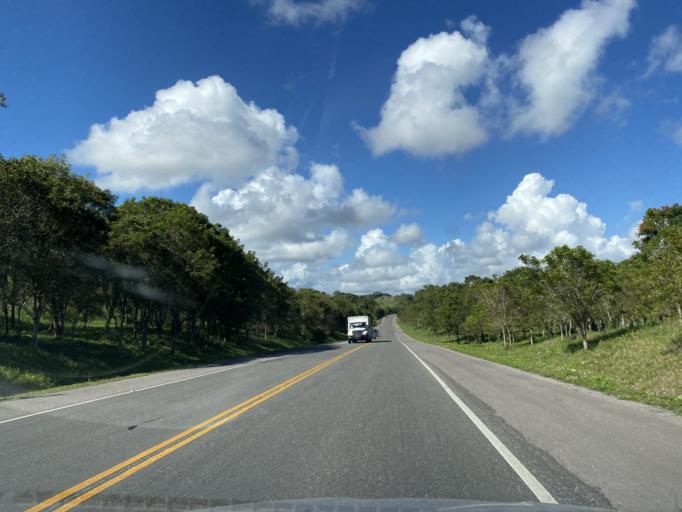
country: DO
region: Monte Plata
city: Majagual
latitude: 19.0277
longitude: -69.8240
